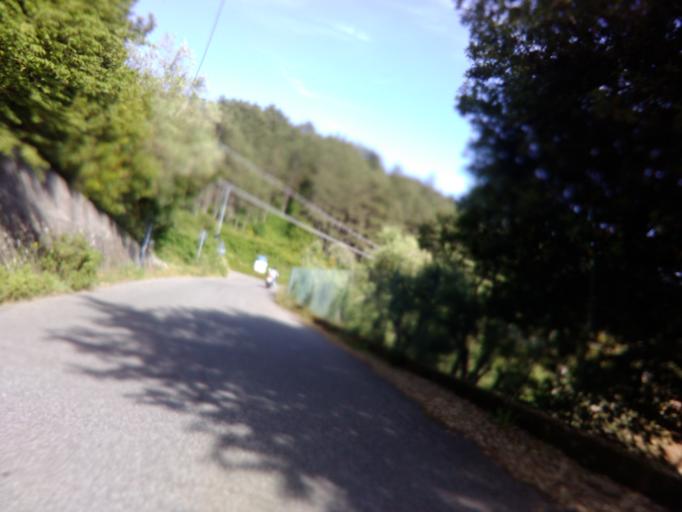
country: IT
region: Tuscany
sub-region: Provincia di Massa-Carrara
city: Fosdinovo
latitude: 44.1468
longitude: 10.0237
